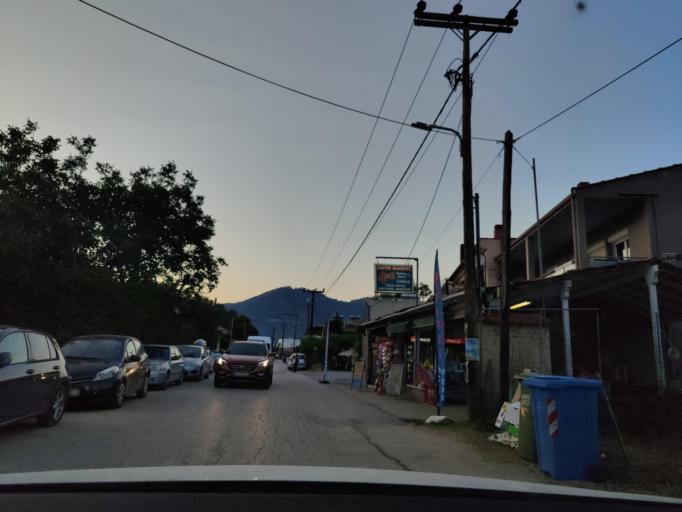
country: GR
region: East Macedonia and Thrace
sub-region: Nomos Kavalas
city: Potamia
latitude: 40.7097
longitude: 24.7583
